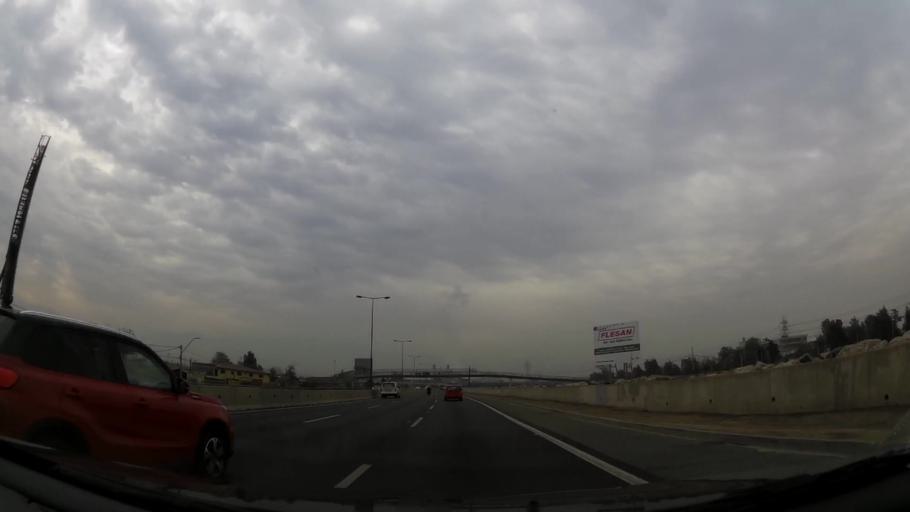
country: CL
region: Santiago Metropolitan
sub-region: Provincia de Santiago
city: Lo Prado
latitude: -33.4125
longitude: -70.6957
